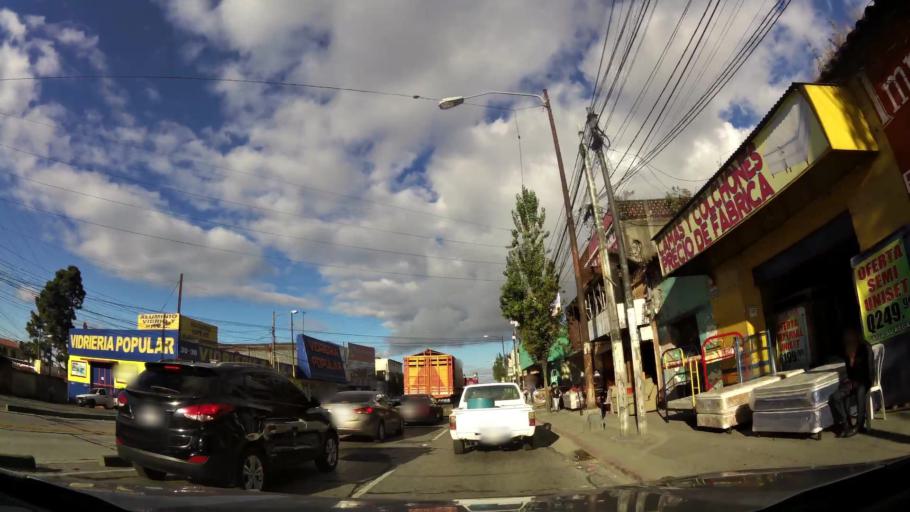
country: GT
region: Guatemala
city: Guatemala City
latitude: 14.6206
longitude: -90.5263
